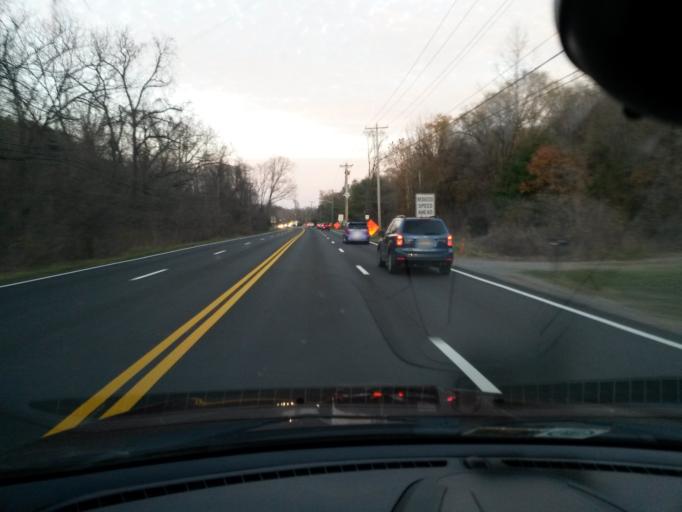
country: US
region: Virginia
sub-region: Botetourt County
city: Daleville
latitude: 37.4029
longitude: -79.8907
